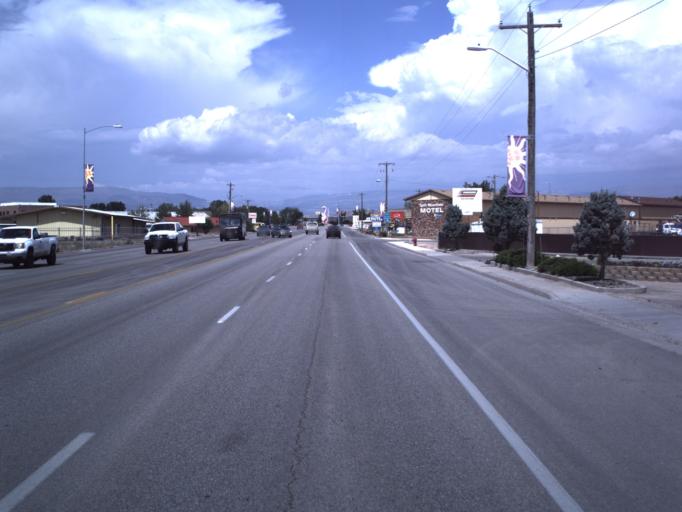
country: US
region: Utah
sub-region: Uintah County
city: Vernal
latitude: 40.4532
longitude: -109.5076
